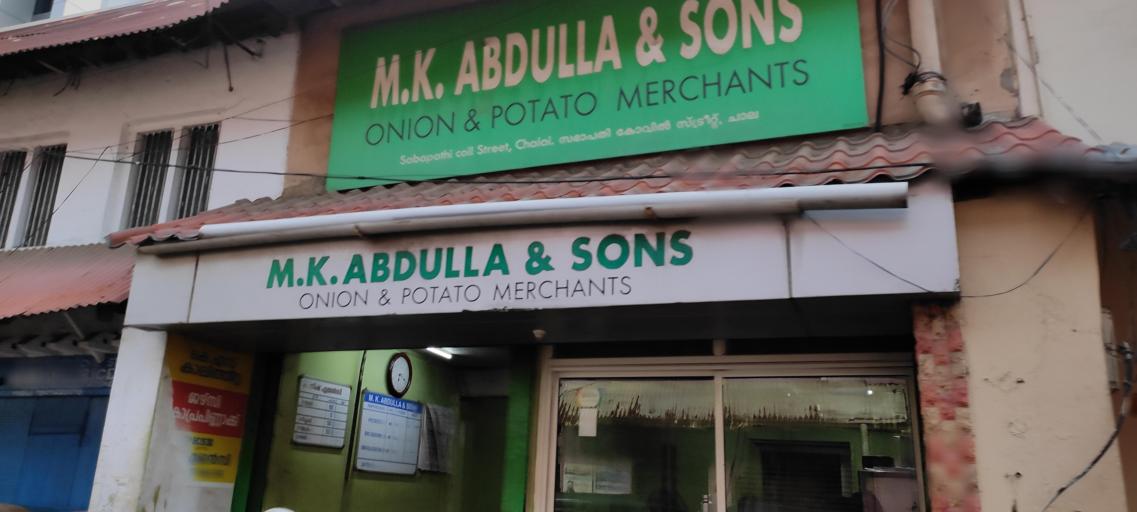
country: IN
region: Kerala
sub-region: Thiruvananthapuram
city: Thiruvananthapuram
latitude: 8.4835
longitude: 76.9507
